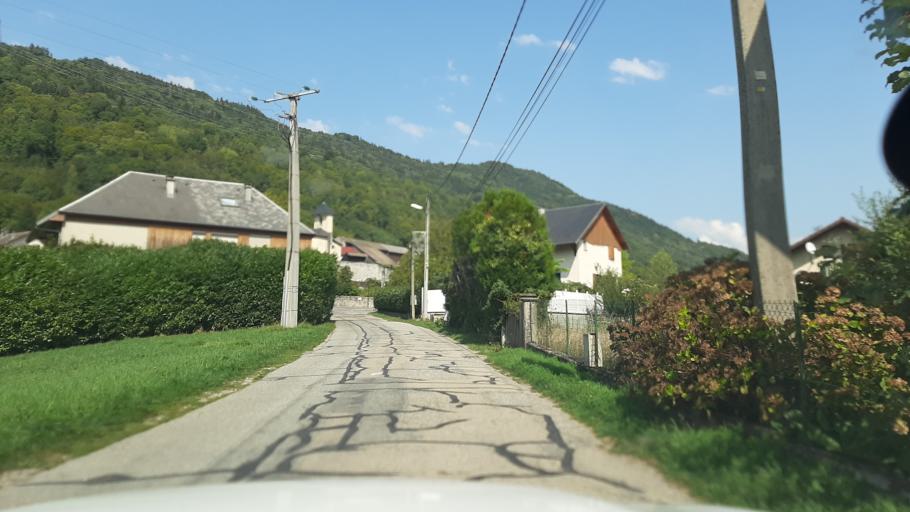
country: FR
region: Rhone-Alpes
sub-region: Departement de la Savoie
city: La Rochette
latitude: 45.4683
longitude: 6.1187
